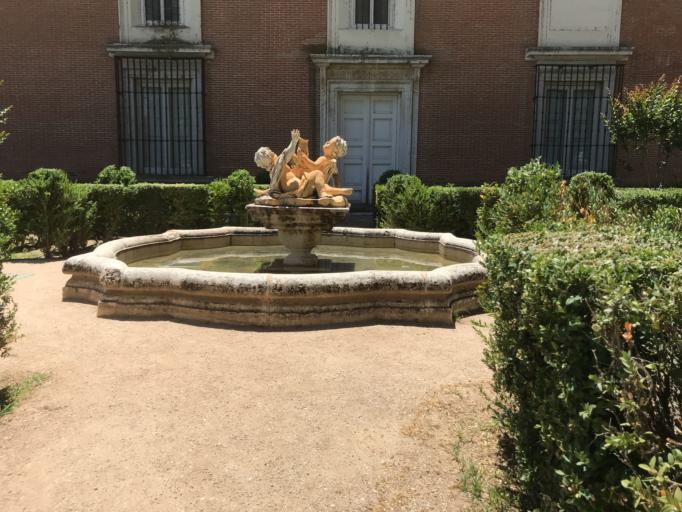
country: ES
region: Madrid
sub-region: Provincia de Madrid
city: Aranjuez
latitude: 40.0368
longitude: -3.6078
